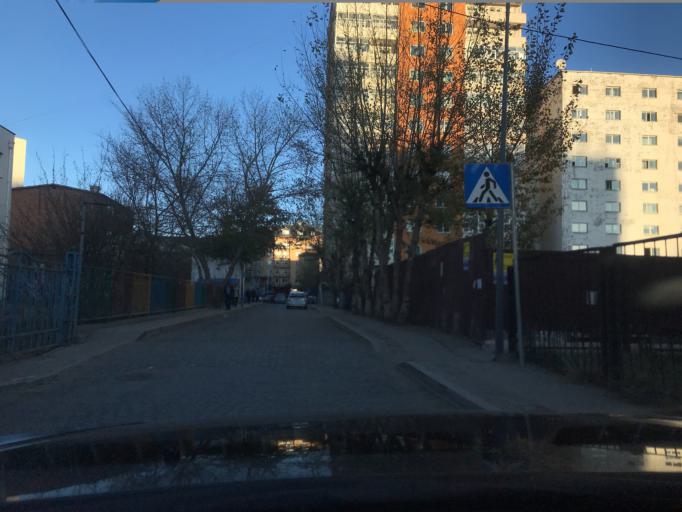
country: MN
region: Ulaanbaatar
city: Ulaanbaatar
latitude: 47.9234
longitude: 106.9084
